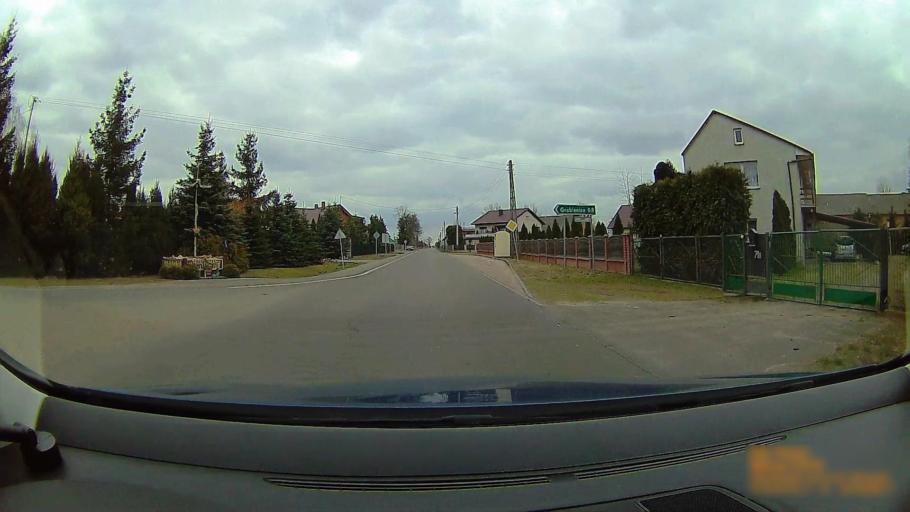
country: PL
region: Greater Poland Voivodeship
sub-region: Powiat koninski
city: Rzgow Pierwszy
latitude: 52.1229
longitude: 18.0666
